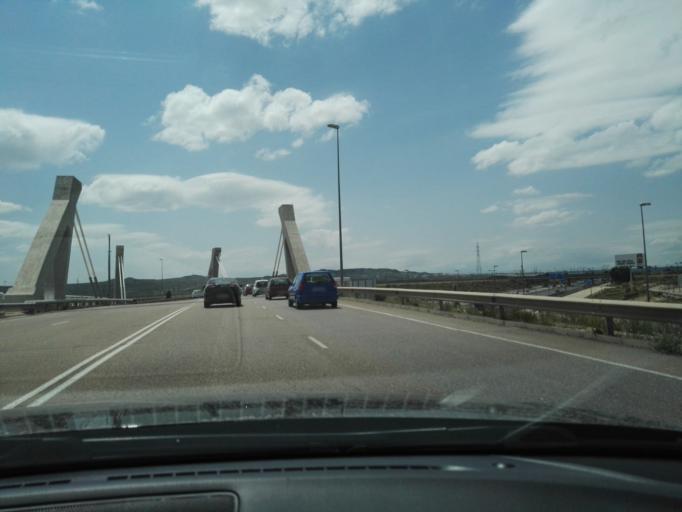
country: ES
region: Aragon
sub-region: Provincia de Zaragoza
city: Montecanal
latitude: 41.6311
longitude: -0.9896
